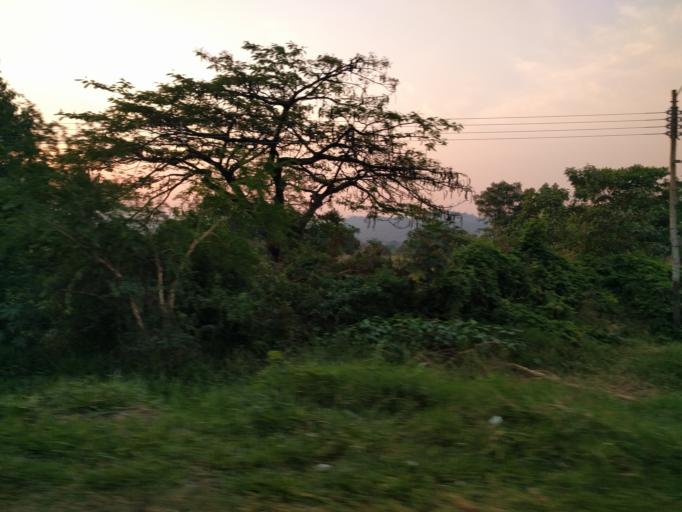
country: BO
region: Santa Cruz
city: Jorochito
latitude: -18.0479
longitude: -63.4205
